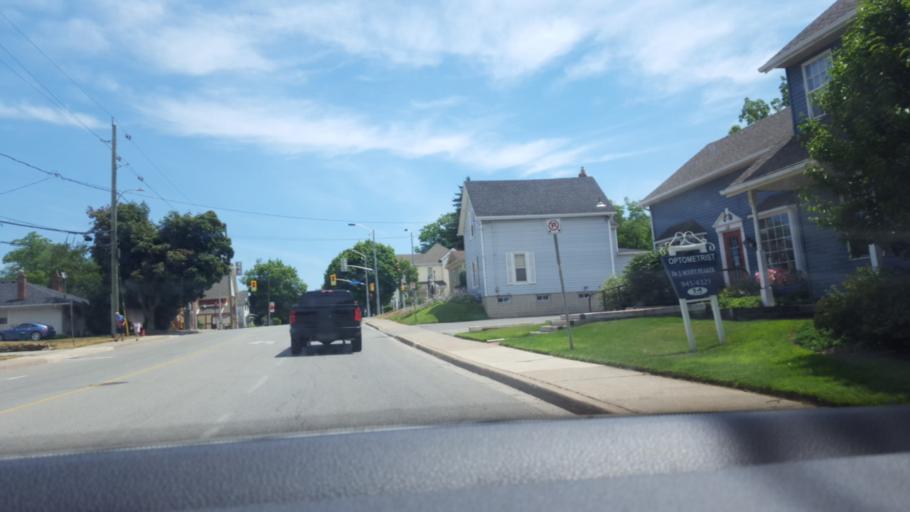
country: CA
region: Ontario
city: Oakville
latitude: 43.1926
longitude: -79.5641
